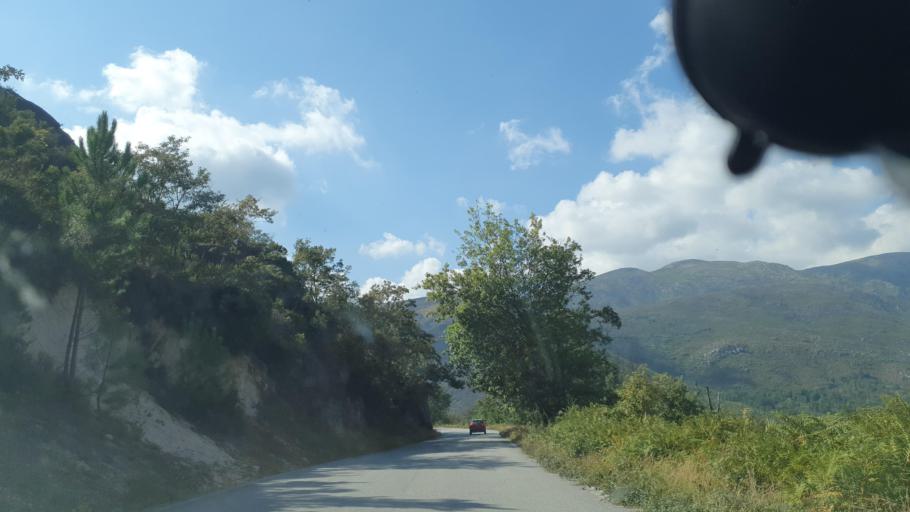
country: PT
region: Braga
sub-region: Terras de Bouro
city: Antas
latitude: 41.7678
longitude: -8.1917
